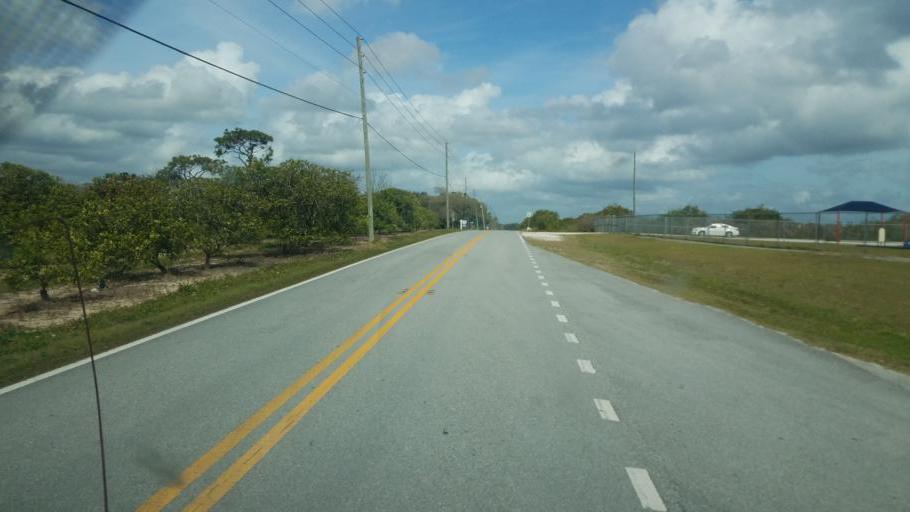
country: US
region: Florida
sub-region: Polk County
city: Dundee
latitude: 28.0439
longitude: -81.5625
